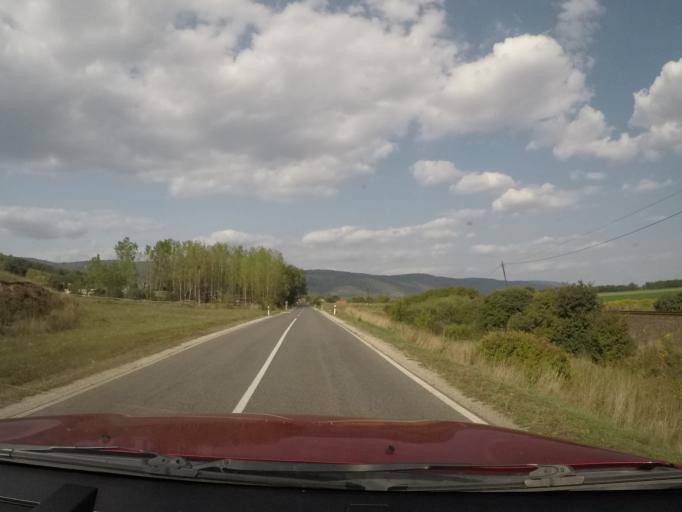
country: HU
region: Borsod-Abauj-Zemplen
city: Szendro
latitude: 48.5285
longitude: 20.7300
